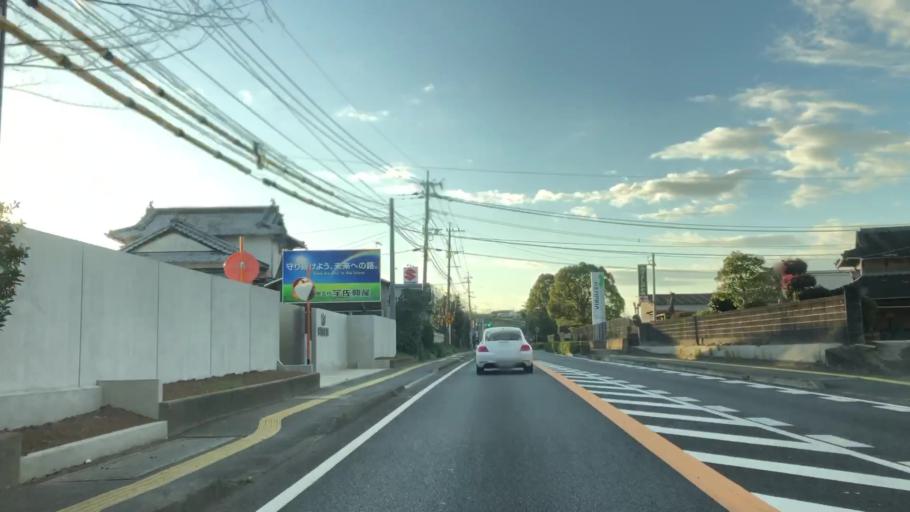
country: JP
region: Oita
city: Bungo-Takada-shi
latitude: 33.5351
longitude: 131.3168
